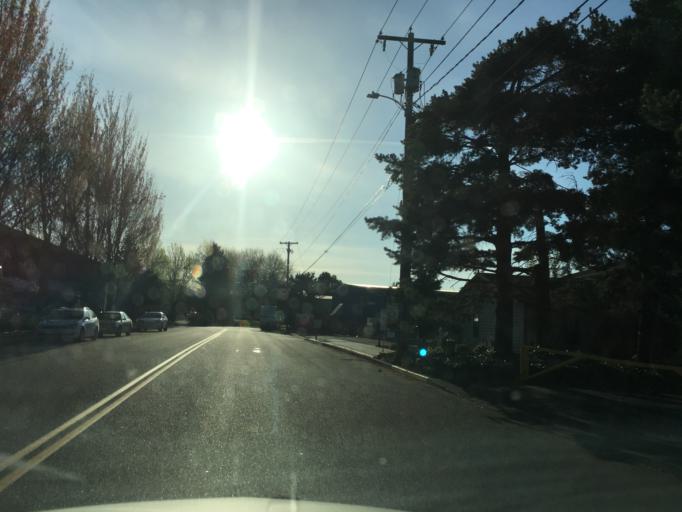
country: US
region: Oregon
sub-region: Multnomah County
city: Lents
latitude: 45.5575
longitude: -122.5228
